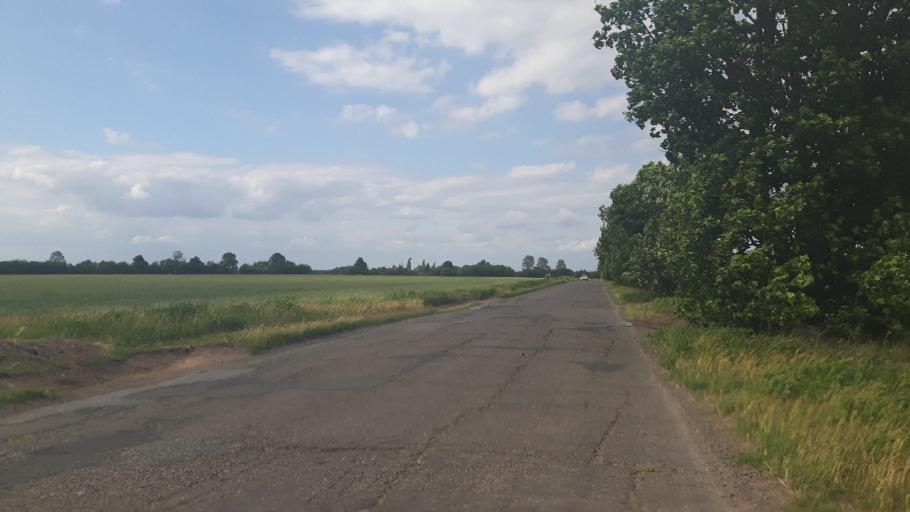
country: DE
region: Brandenburg
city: Rudnitz
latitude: 52.6880
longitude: 13.6576
